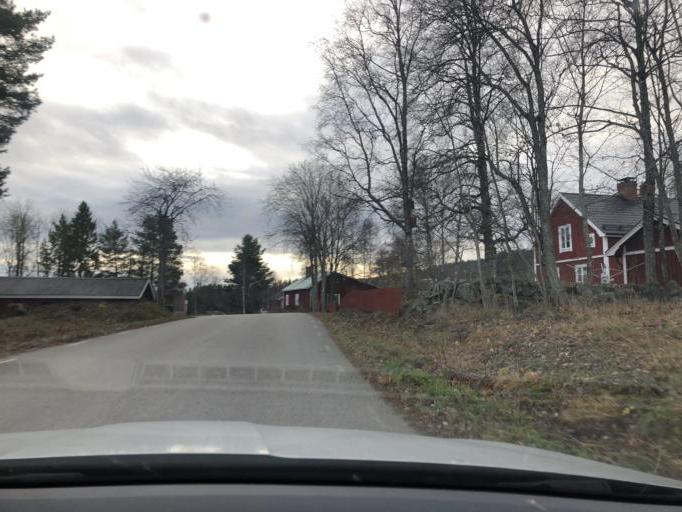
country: SE
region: Gaevleborg
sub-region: Hudiksvalls Kommun
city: Sorforsa
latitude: 61.6762
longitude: 16.9241
